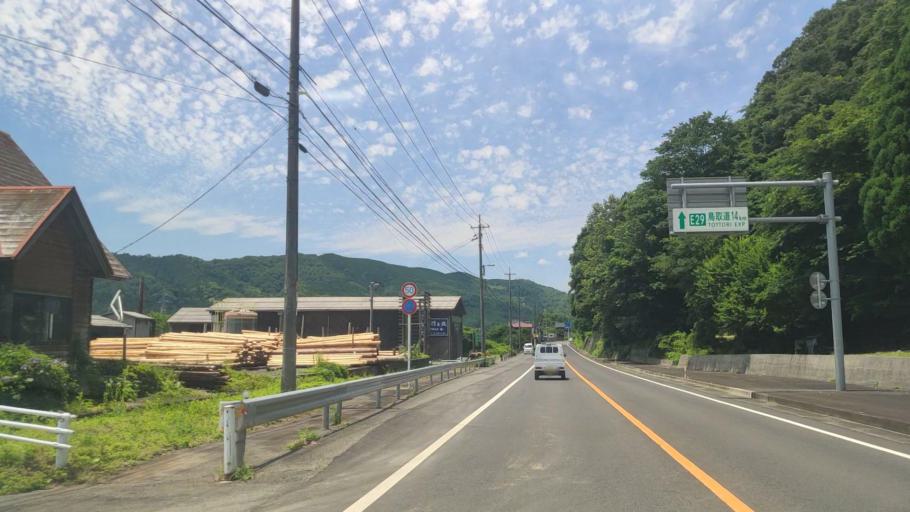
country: JP
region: Tottori
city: Tottori
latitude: 35.3664
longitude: 134.3226
